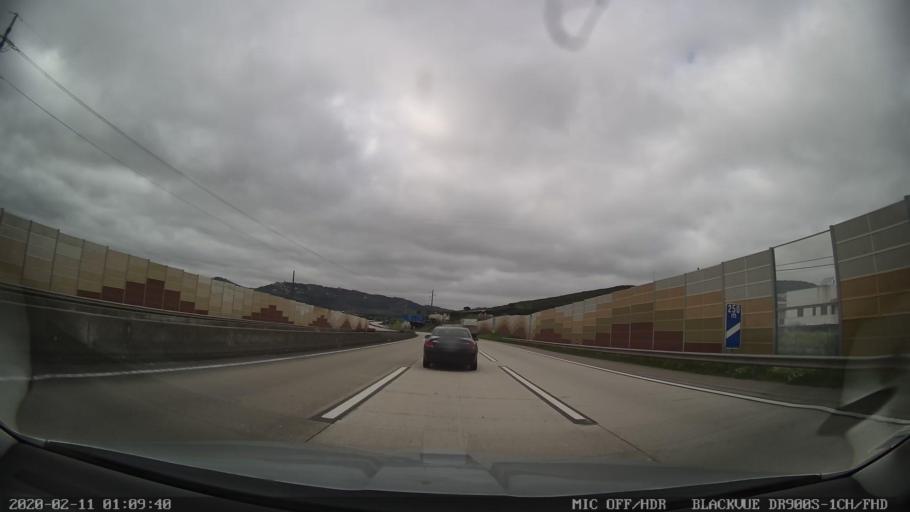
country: PT
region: Lisbon
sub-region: Loures
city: Loures
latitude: 38.8557
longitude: -9.1685
